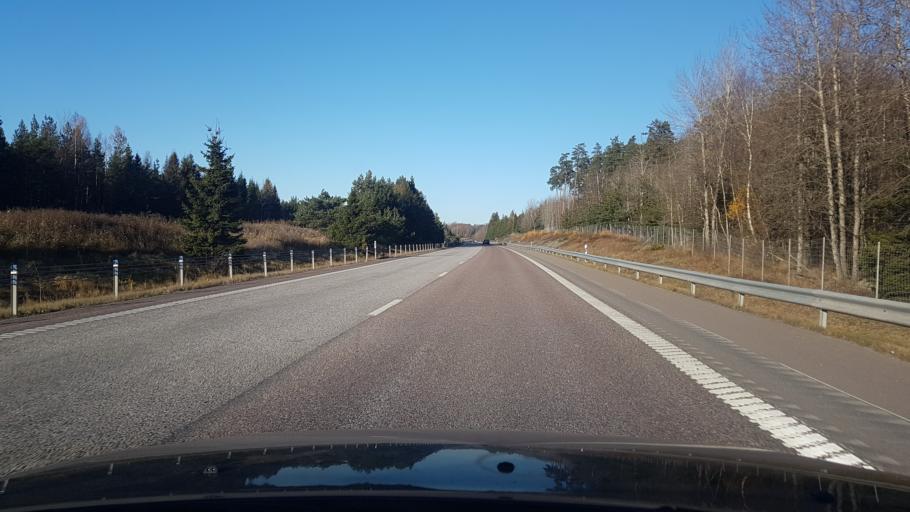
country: SE
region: Uppsala
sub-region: Uppsala Kommun
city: Alsike
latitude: 59.7715
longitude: 17.7874
